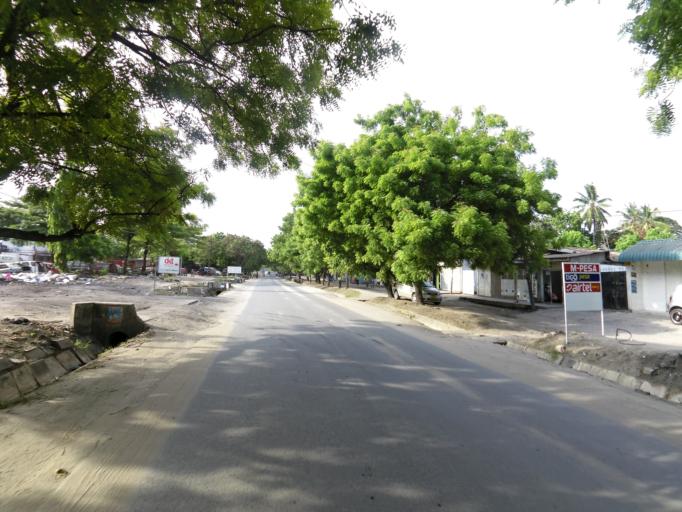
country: TZ
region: Dar es Salaam
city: Magomeni
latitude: -6.7766
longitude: 39.2415
